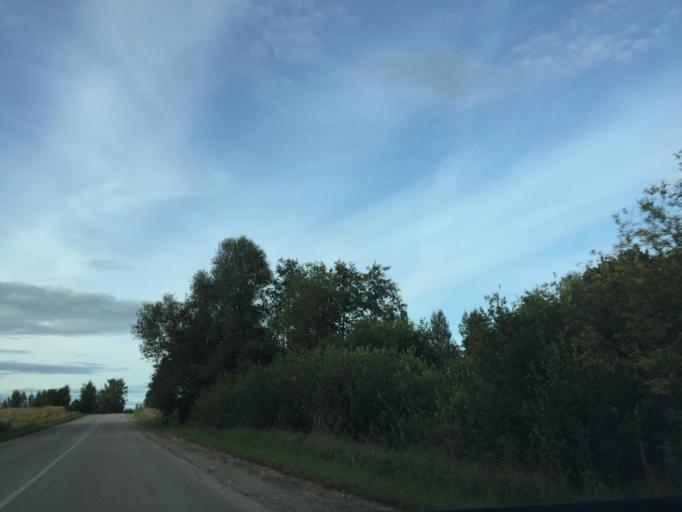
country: LV
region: Viesite
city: Viesite
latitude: 56.3113
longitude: 25.4479
